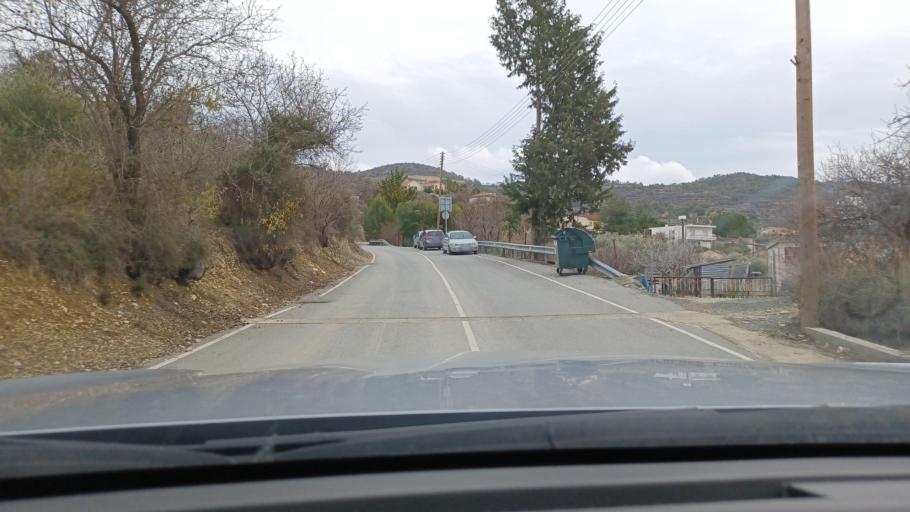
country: CY
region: Limassol
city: Pelendri
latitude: 34.8106
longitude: 32.9099
